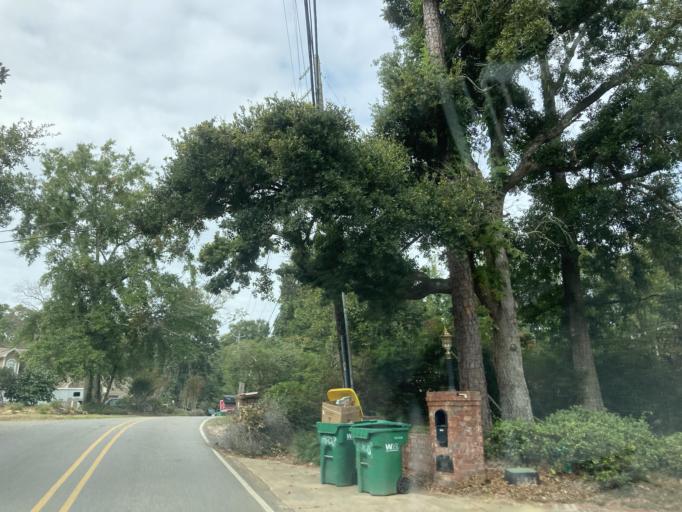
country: US
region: Mississippi
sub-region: Jackson County
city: Gulf Hills
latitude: 30.4361
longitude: -88.8408
